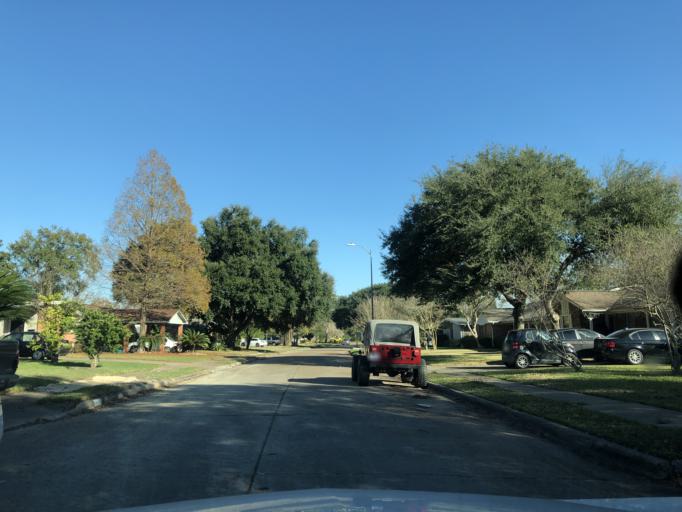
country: US
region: Texas
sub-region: Harris County
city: Bellaire
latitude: 29.6980
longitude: -95.5099
